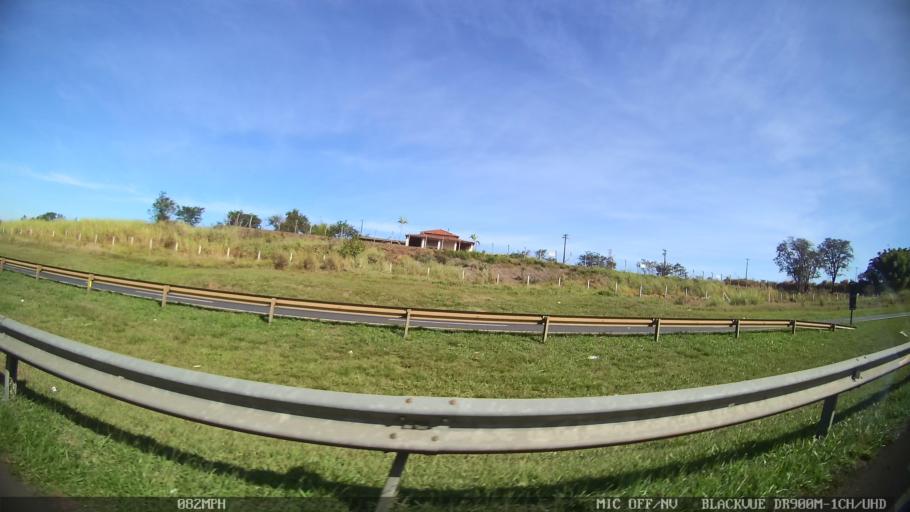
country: BR
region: Sao Paulo
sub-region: Pirassununga
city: Pirassununga
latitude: -22.0891
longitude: -47.4192
